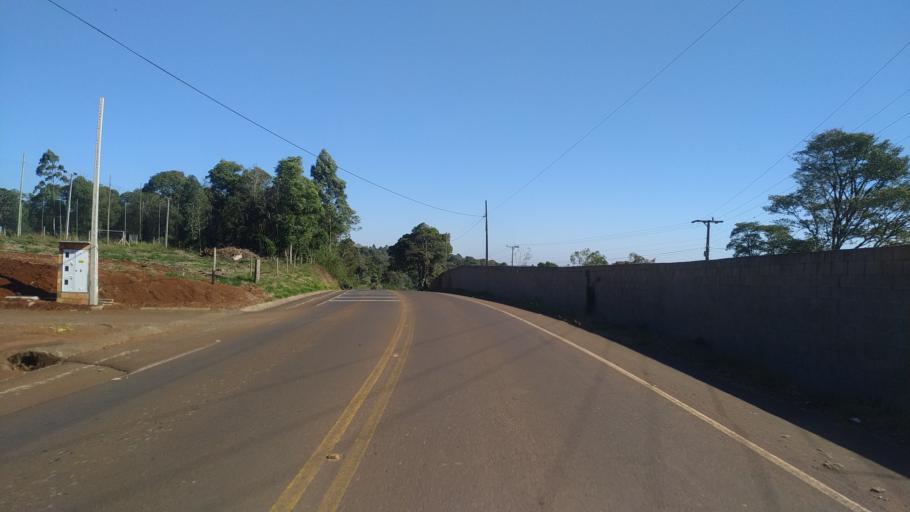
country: BR
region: Santa Catarina
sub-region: Chapeco
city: Chapeco
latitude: -27.1582
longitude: -52.6084
